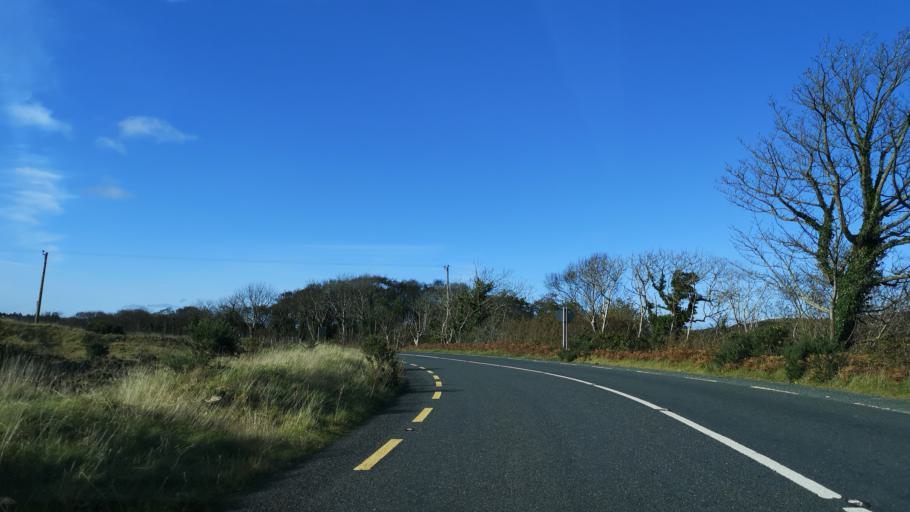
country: IE
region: Connaught
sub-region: County Galway
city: Clifden
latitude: 53.5614
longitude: -9.9238
